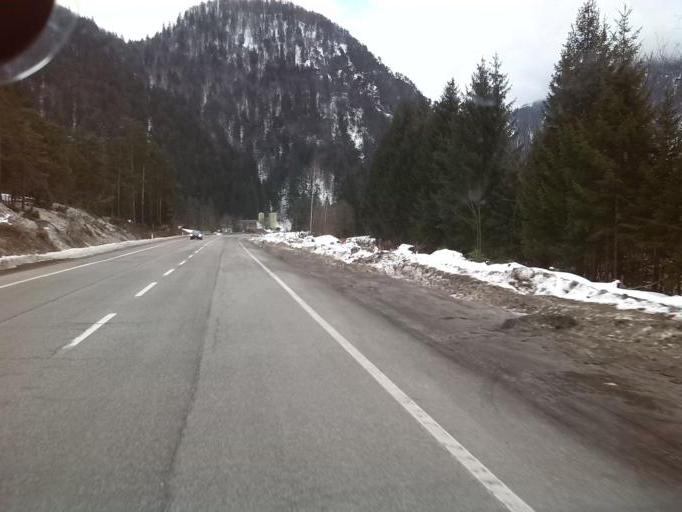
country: IT
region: Friuli Venezia Giulia
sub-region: Provincia di Udine
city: Malborghetto
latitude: 46.5084
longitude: 13.4865
